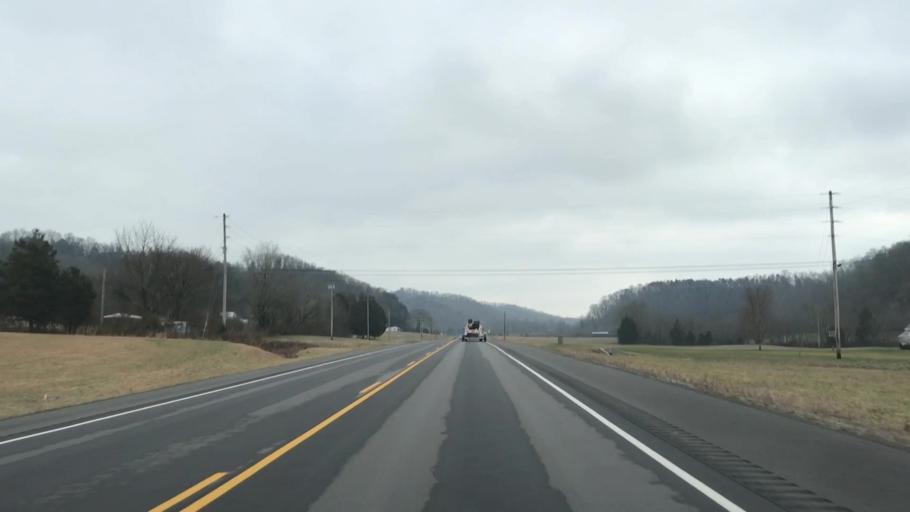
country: US
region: Kentucky
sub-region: Cumberland County
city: Burkesville
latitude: 36.8419
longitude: -85.3707
